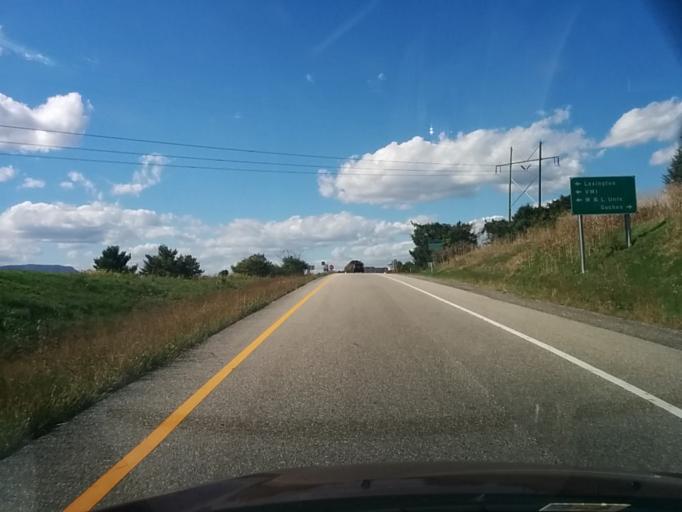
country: US
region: Virginia
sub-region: Rockbridge County
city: East Lexington
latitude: 37.8005
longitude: -79.4119
